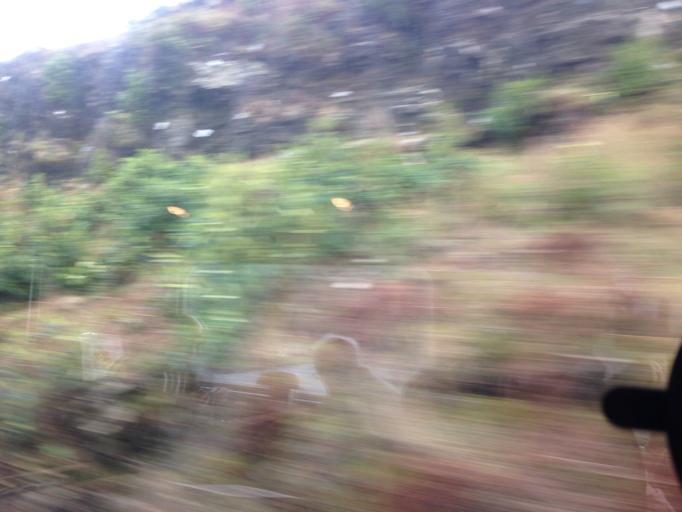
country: GB
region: Scotland
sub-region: Argyll and Bute
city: Garelochhead
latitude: 56.1791
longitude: -4.7726
